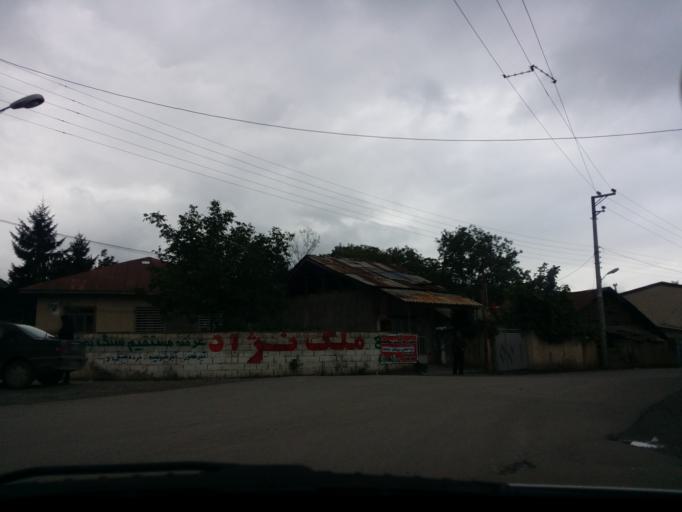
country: IR
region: Mazandaran
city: `Abbasabad
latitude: 36.5053
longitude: 51.1869
